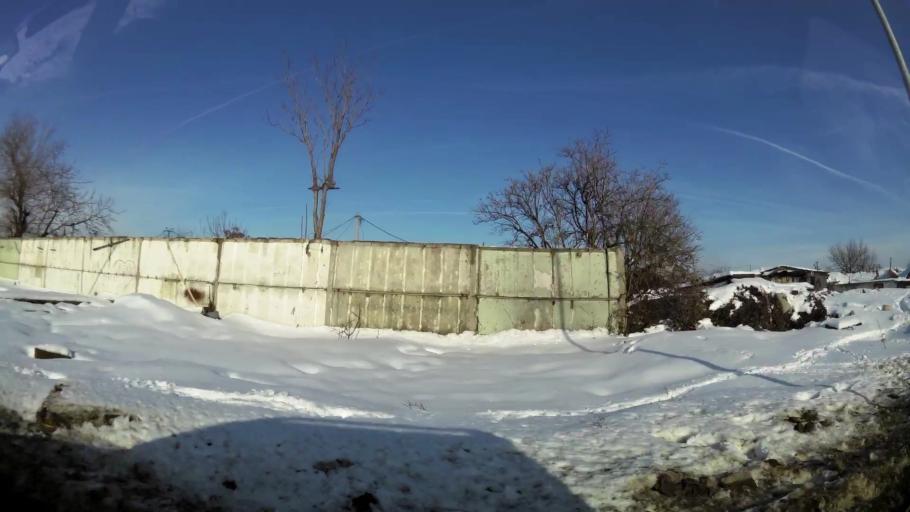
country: RS
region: Central Serbia
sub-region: Belgrade
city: Palilula
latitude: 44.8218
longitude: 20.4958
